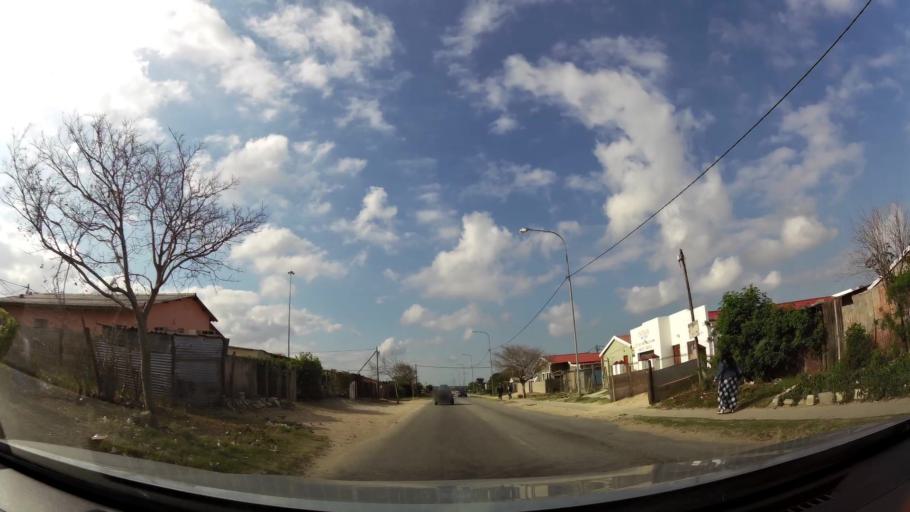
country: ZA
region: Eastern Cape
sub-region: Nelson Mandela Bay Metropolitan Municipality
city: Port Elizabeth
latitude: -33.7872
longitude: 25.5878
